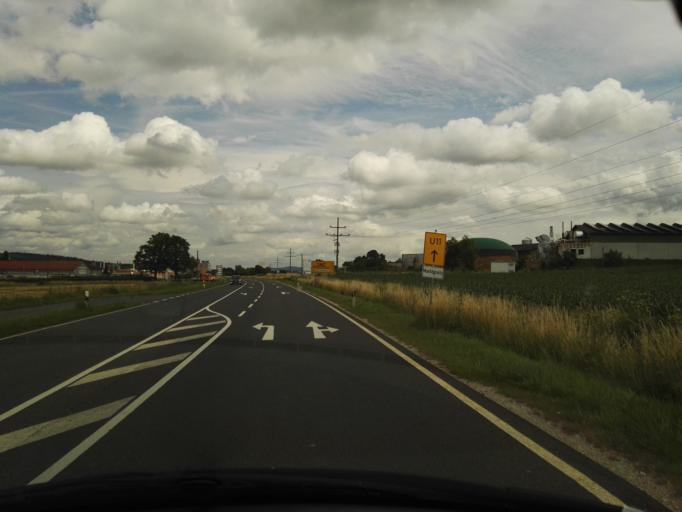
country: DE
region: Bavaria
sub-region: Upper Franconia
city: Redwitz an der Rodach
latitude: 50.1658
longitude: 11.2025
